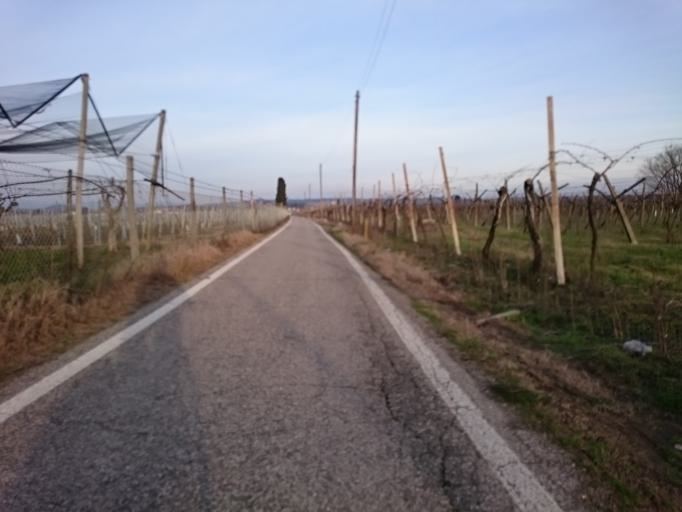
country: IT
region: Veneto
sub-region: Provincia di Verona
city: Cola
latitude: 45.4565
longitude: 10.7448
